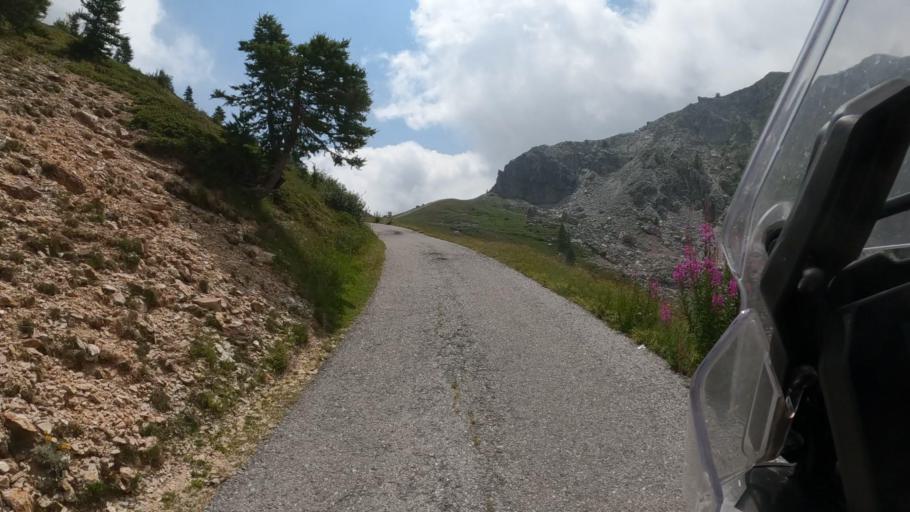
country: IT
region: Piedmont
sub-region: Provincia di Cuneo
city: Marmora
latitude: 44.3976
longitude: 7.1217
